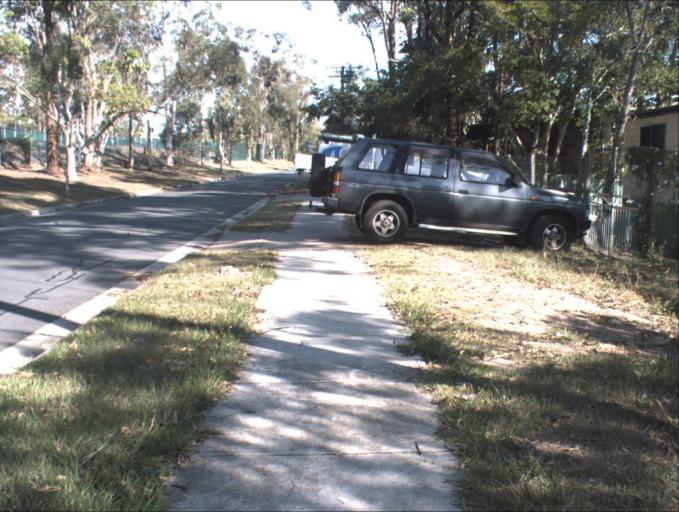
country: AU
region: Queensland
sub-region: Logan
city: Woodridge
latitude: -27.6247
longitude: 153.0985
